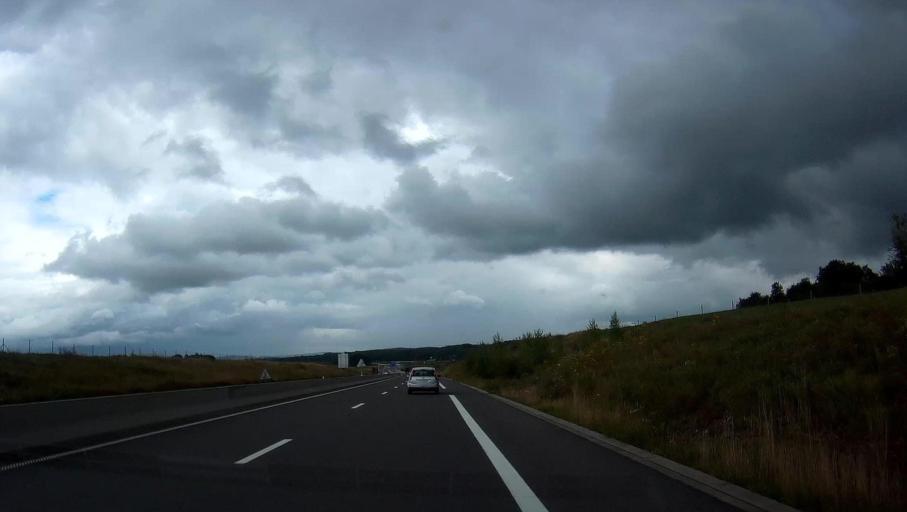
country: FR
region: Champagne-Ardenne
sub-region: Departement des Ardennes
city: Tournes
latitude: 49.7713
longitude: 4.6277
